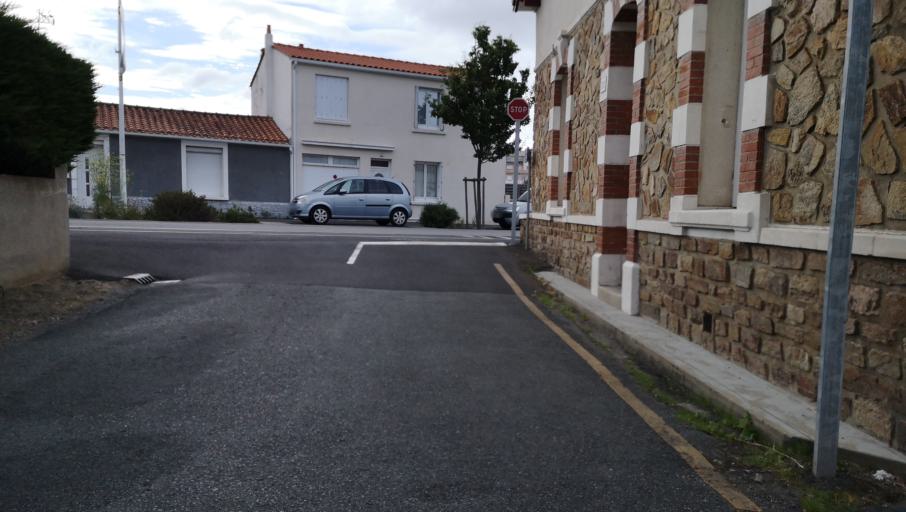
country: FR
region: Pays de la Loire
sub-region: Departement de la Vendee
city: Les Sables-d'Olonne
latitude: 46.5082
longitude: -1.7775
